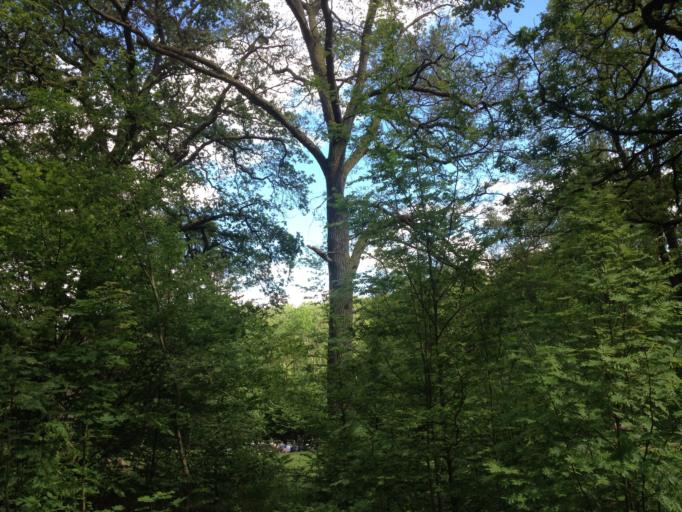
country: SE
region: Skane
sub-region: Klippans Kommun
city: Ljungbyhed
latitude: 56.0384
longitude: 13.2513
